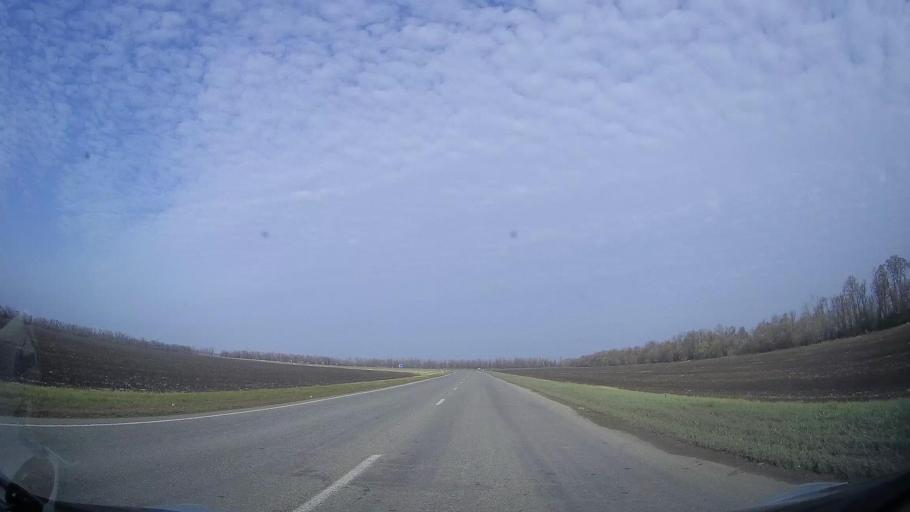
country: RU
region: Rostov
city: Tselina
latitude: 46.5250
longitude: 40.9914
